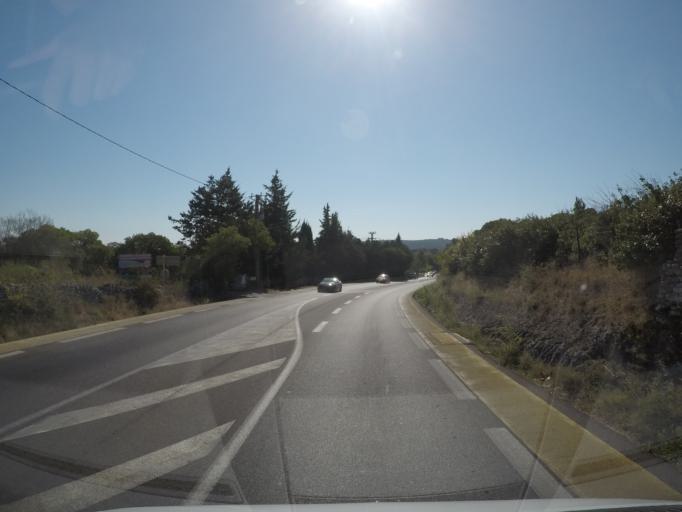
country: FR
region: Languedoc-Roussillon
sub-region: Departement du Gard
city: Uzes
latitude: 43.9946
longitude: 4.4186
